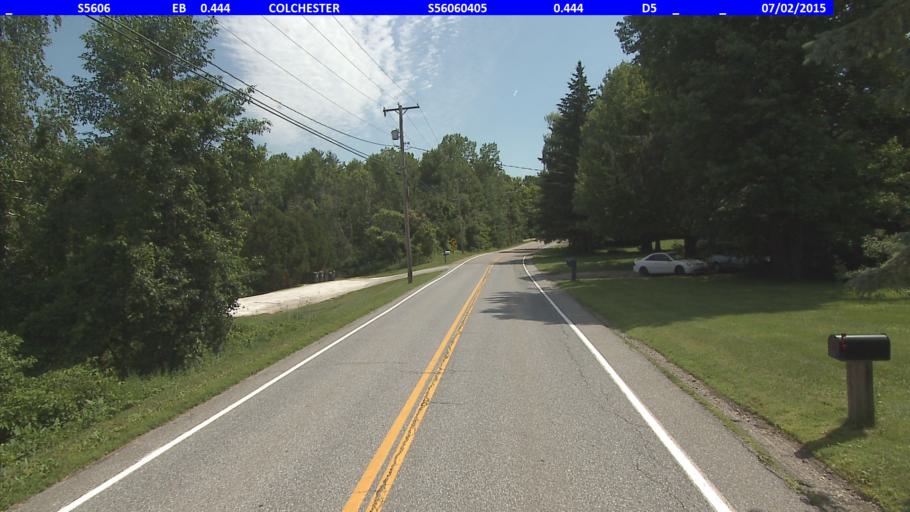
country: US
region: Vermont
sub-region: Chittenden County
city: Burlington
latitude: 44.5530
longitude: -73.2411
